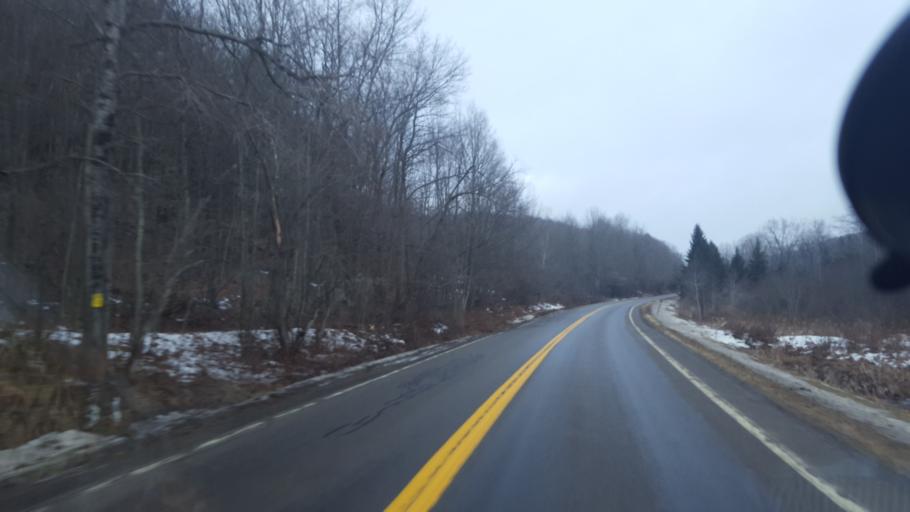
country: US
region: New York
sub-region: Allegany County
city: Andover
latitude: 42.0801
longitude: -77.6742
